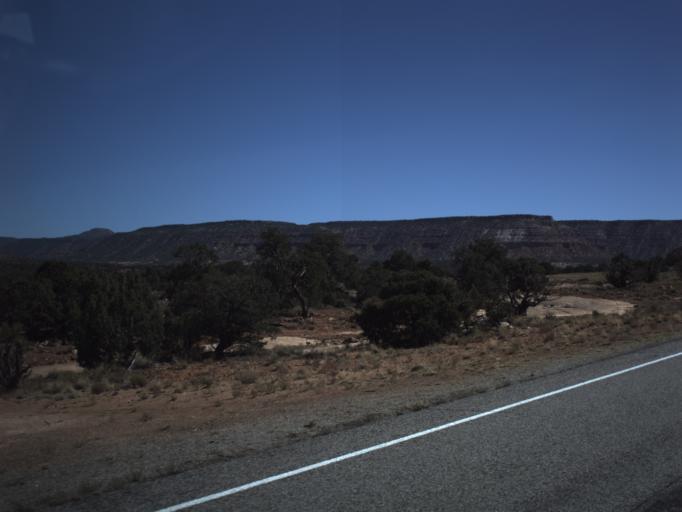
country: US
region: Utah
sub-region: San Juan County
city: Blanding
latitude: 37.6344
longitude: -110.1003
